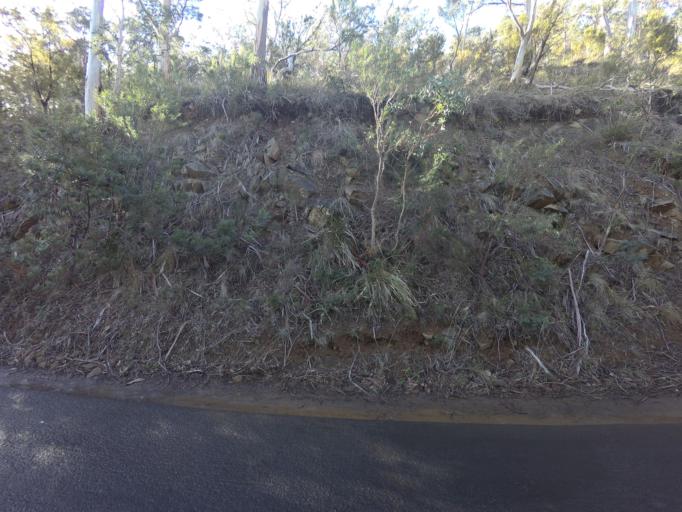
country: AU
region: Tasmania
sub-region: Glenorchy
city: Berriedale
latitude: -42.8202
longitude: 147.1797
